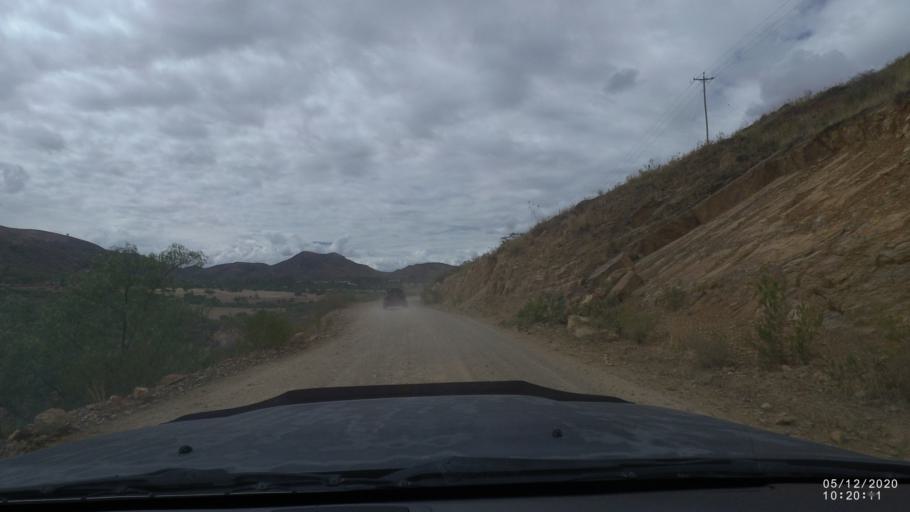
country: BO
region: Cochabamba
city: Sipe Sipe
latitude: -17.4822
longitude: -66.2832
